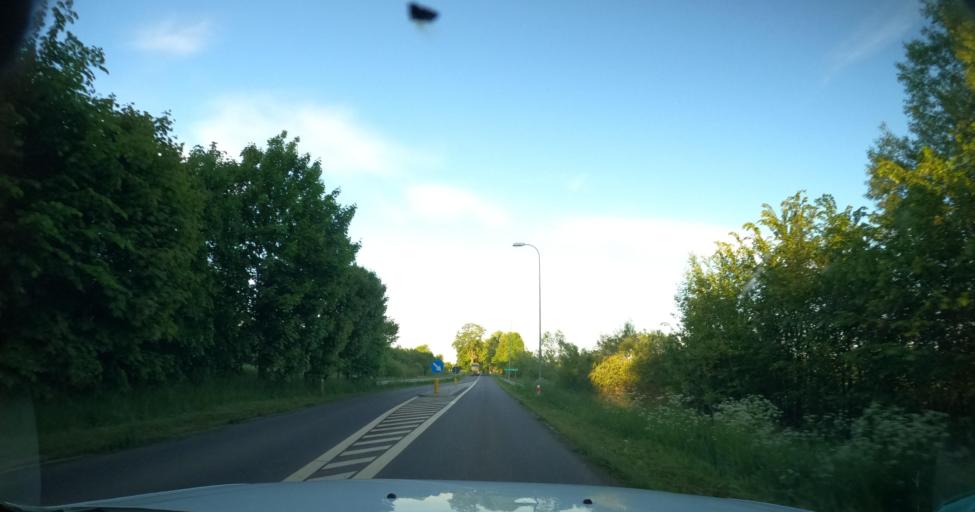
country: PL
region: Warmian-Masurian Voivodeship
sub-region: Powiat lidzbarski
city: Lidzbark Warminski
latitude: 54.1457
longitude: 20.4825
